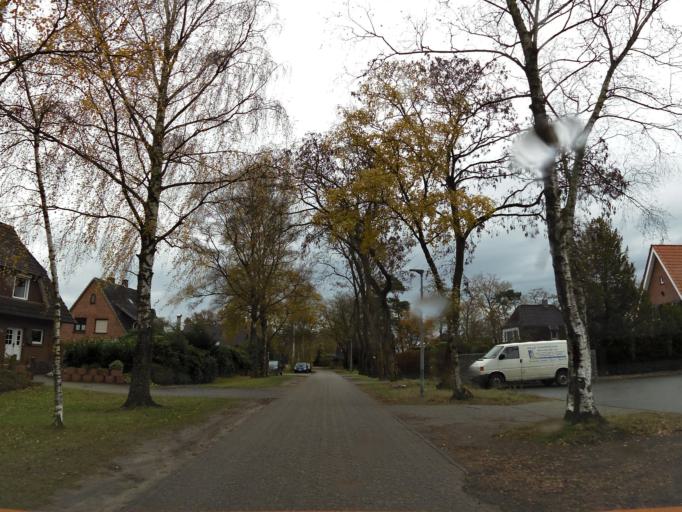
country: DE
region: Lower Saxony
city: Hude
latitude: 53.1012
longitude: 8.4732
